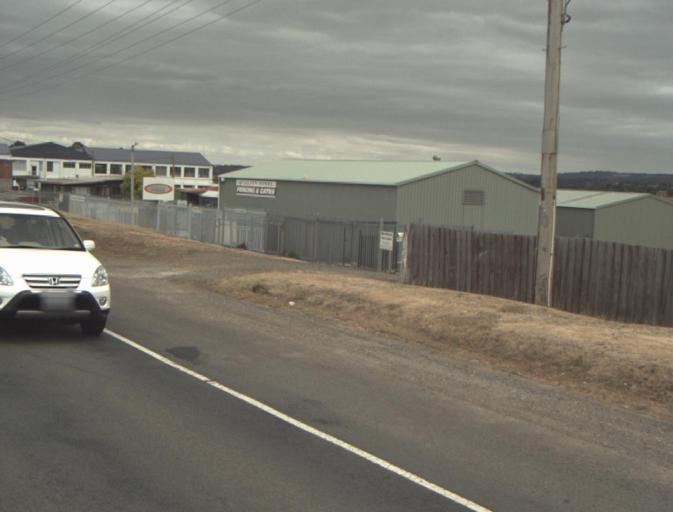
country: AU
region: Tasmania
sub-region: Launceston
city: Newstead
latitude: -41.4473
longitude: 147.1865
